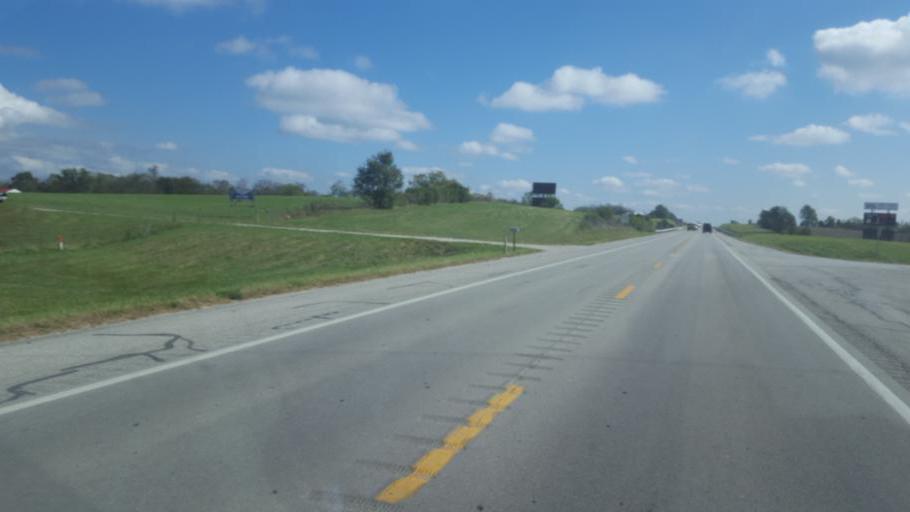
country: US
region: Kentucky
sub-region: Mason County
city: Maysville
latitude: 38.5996
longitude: -83.7407
